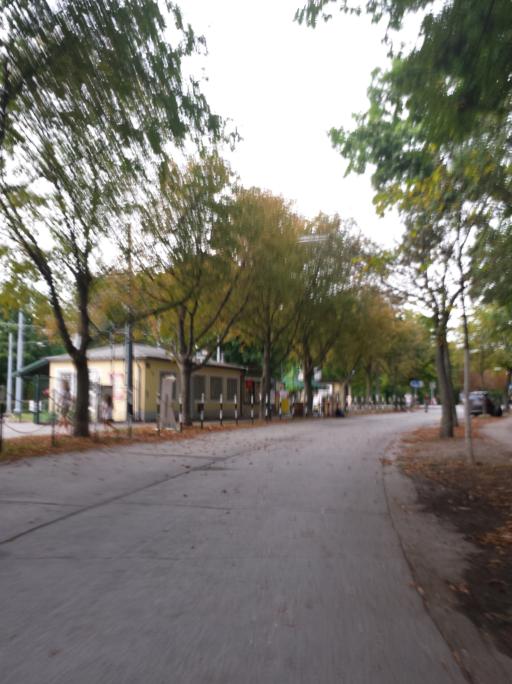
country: AT
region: Vienna
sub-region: Wien Stadt
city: Vienna
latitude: 48.2088
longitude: 16.4062
